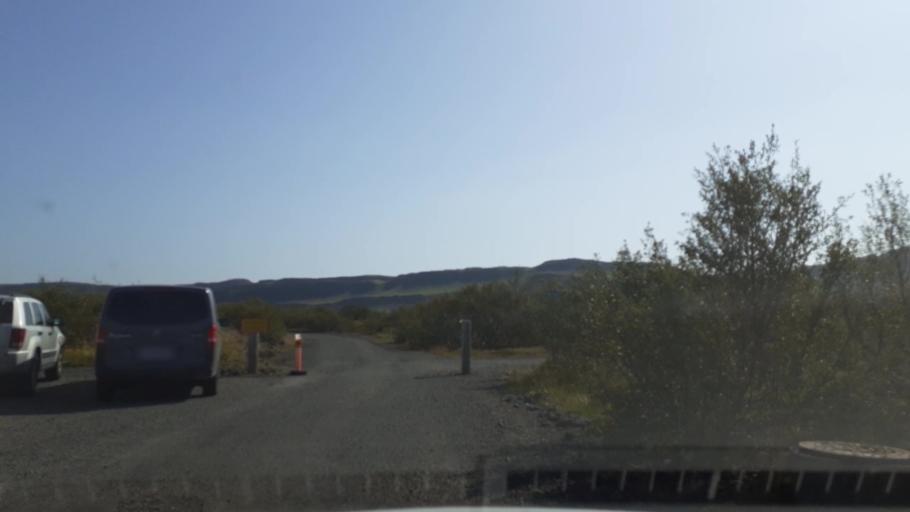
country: IS
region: West
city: Borgarnes
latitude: 64.7557
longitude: -21.5480
